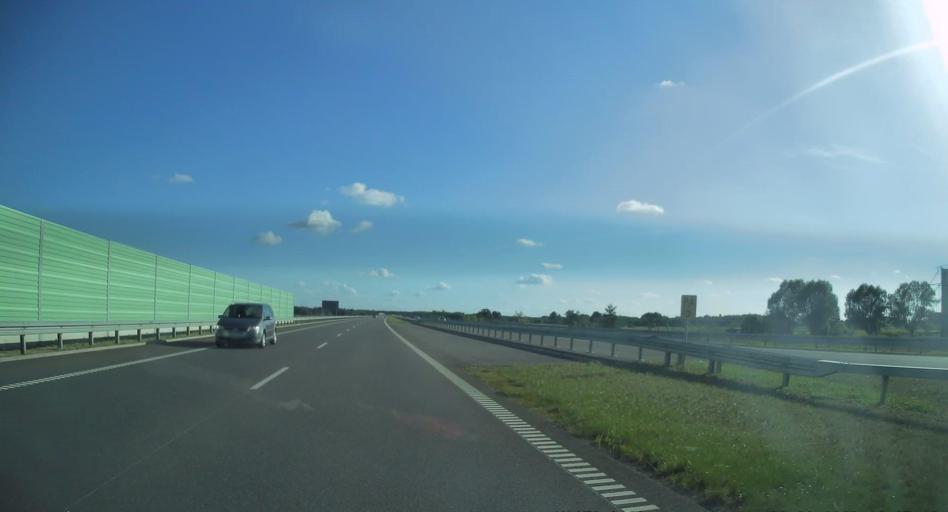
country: PL
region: Masovian Voivodeship
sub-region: Powiat radomski
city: Jedlinsk
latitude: 51.5053
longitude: 21.0811
